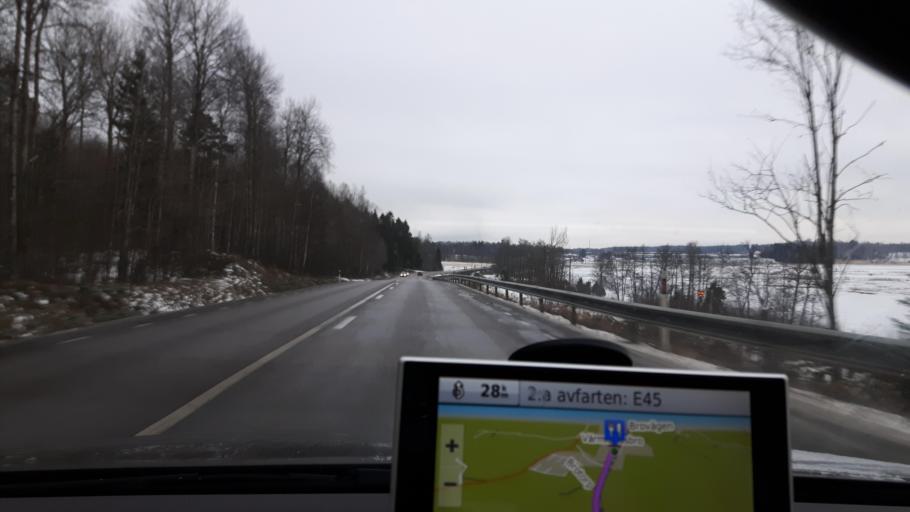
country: SE
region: Vaermland
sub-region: Saffle Kommun
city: Saeffle
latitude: 59.1995
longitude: 13.0248
